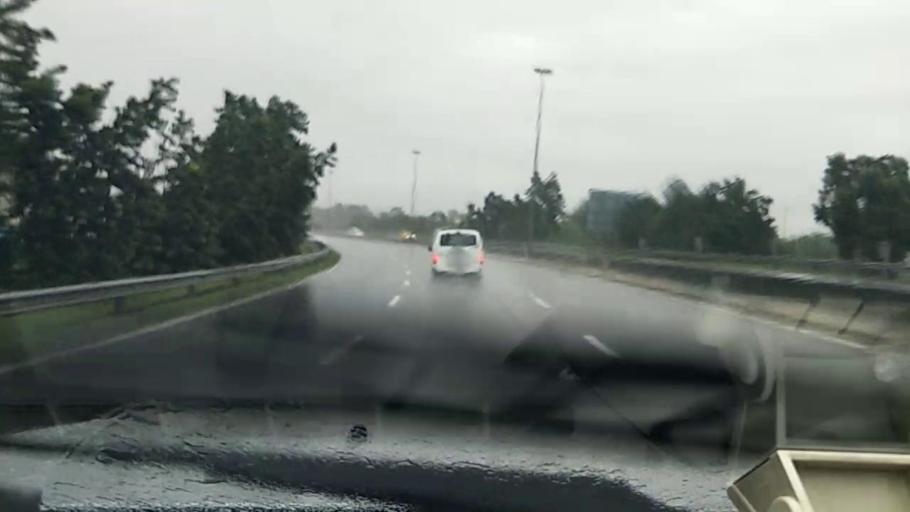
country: MY
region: Selangor
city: Kampong Baharu Balakong
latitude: 2.9989
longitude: 101.7752
